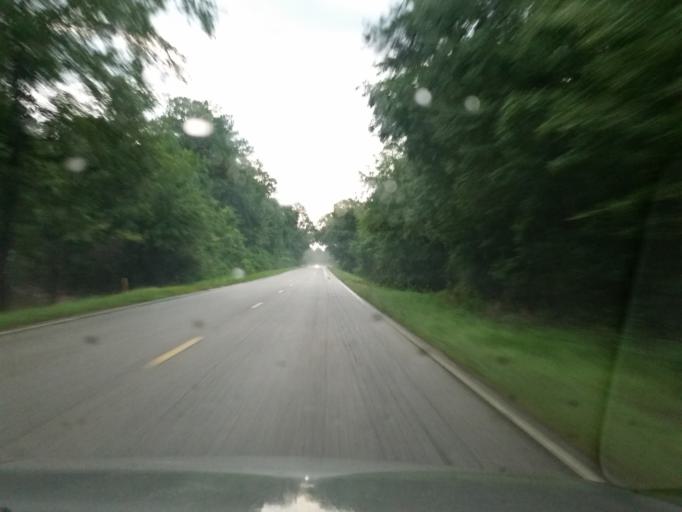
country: US
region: Florida
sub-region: Escambia County
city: Cantonment
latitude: 30.6061
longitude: -87.4071
